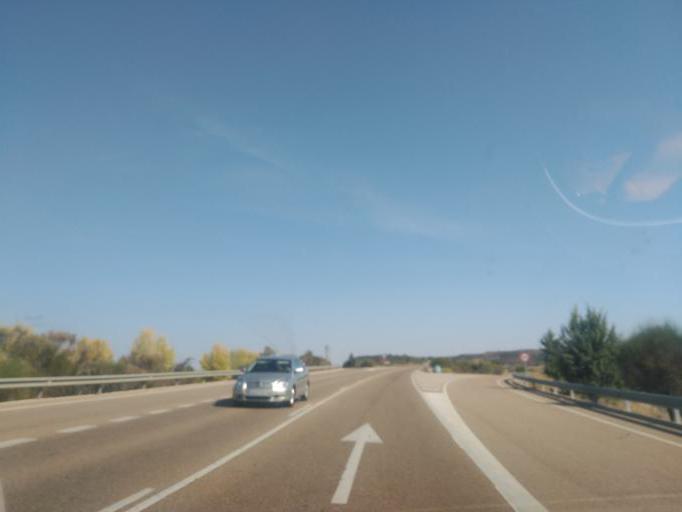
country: ES
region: Castille and Leon
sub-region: Provincia de Valladolid
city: Quintanilla de Arriba
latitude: 41.6201
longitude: -4.2305
